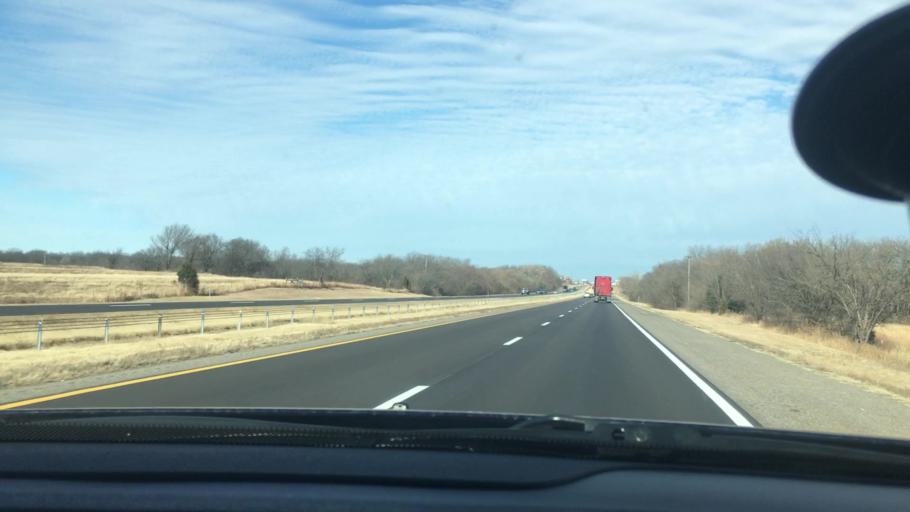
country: US
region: Oklahoma
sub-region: McClain County
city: Goldsby
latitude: 35.1298
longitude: -97.4550
